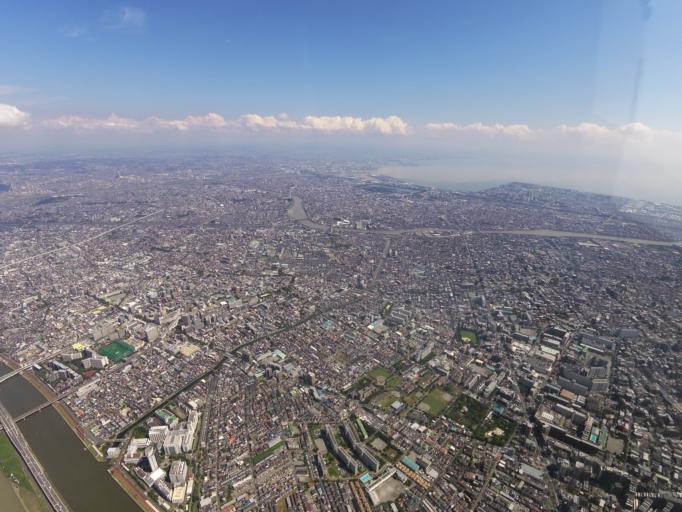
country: JP
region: Tokyo
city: Urayasu
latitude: 35.6756
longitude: 139.8482
